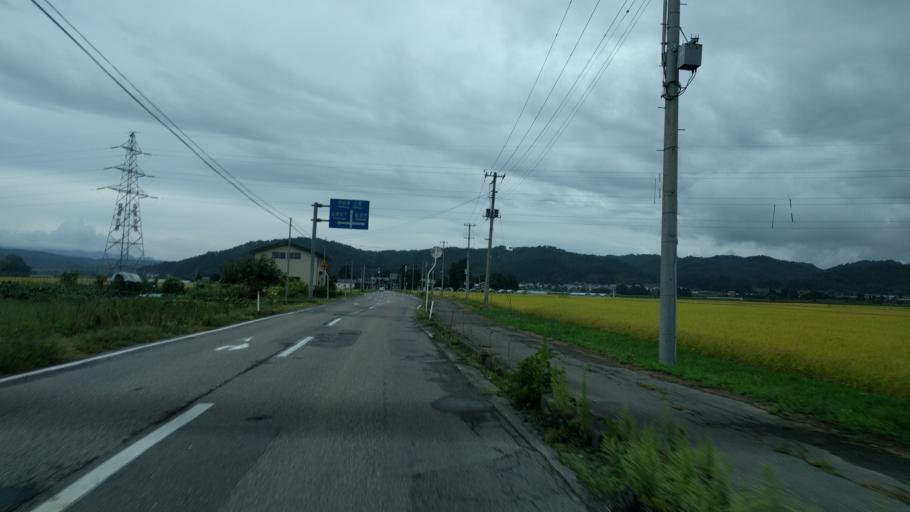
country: JP
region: Fukushima
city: Kitakata
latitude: 37.6122
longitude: 139.8473
